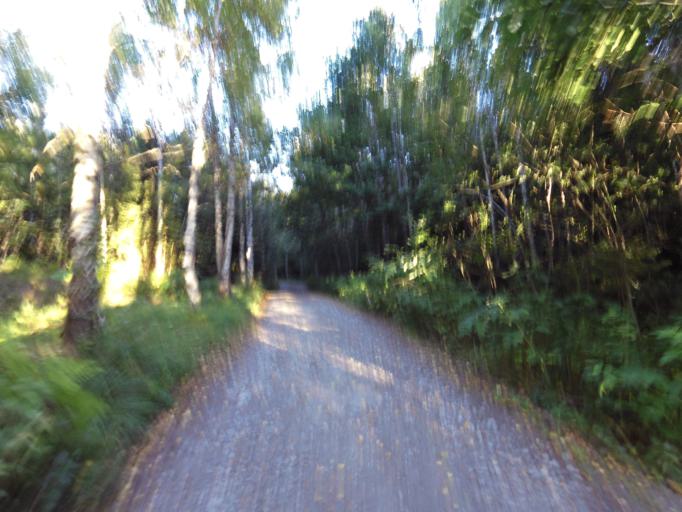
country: SE
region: Gaevleborg
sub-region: Gavle Kommun
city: Gavle
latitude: 60.7221
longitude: 17.1401
